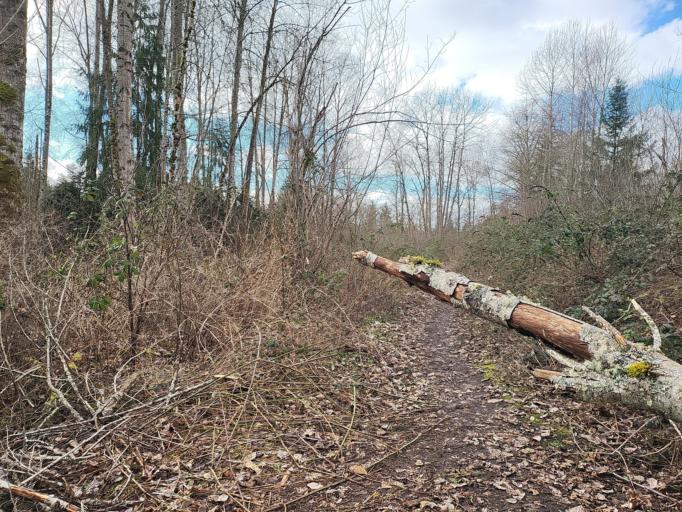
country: US
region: Washington
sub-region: King County
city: Fairwood
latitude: 47.4692
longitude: -122.1509
